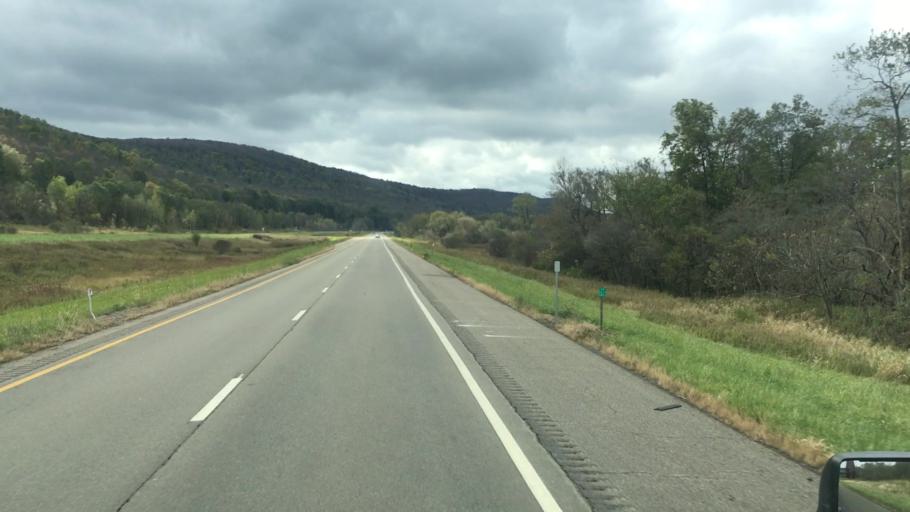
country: US
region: New York
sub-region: Allegany County
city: Cuba
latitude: 42.1937
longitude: -78.3368
